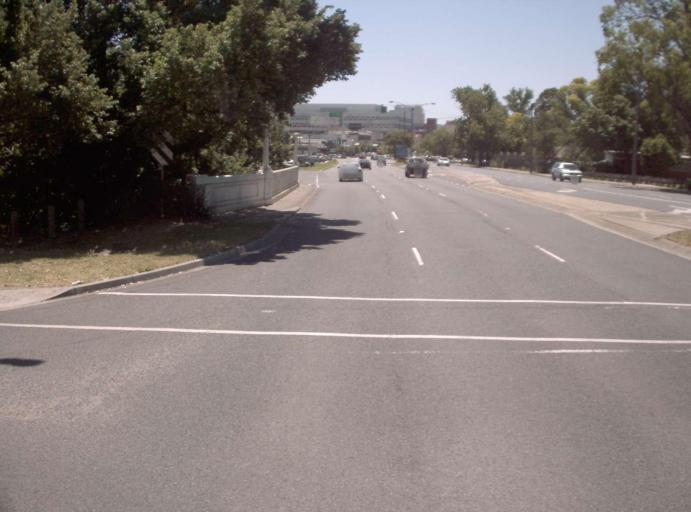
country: AU
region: Victoria
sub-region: Greater Dandenong
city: Dandenong
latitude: -37.9928
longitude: 145.2159
